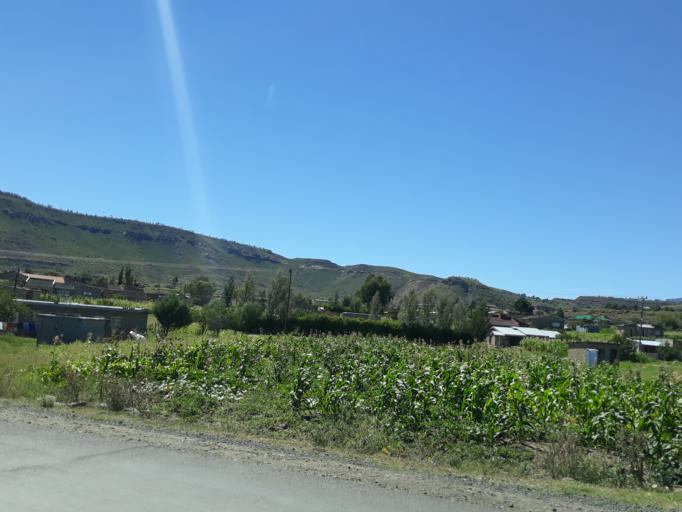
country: LS
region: Mohale's Hoek District
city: Mohale's Hoek
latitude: -30.1104
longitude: 27.4695
